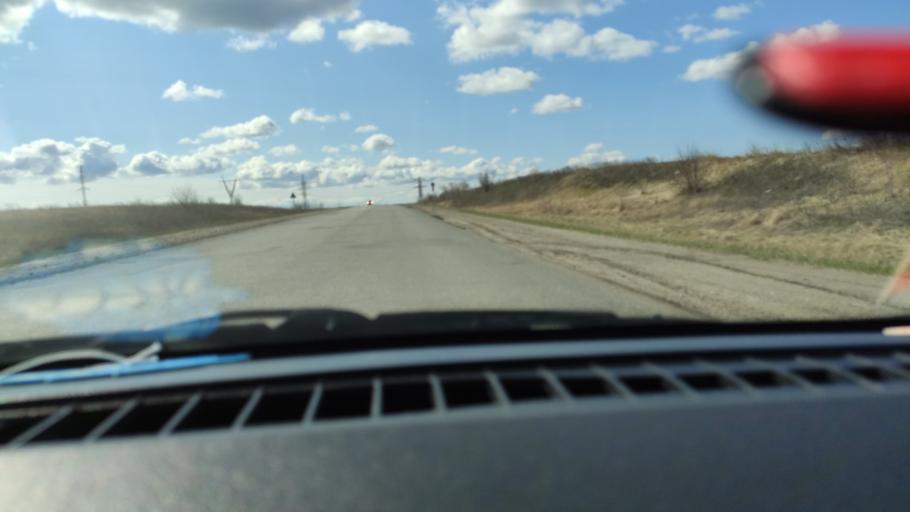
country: RU
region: Samara
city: Varlamovo
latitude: 53.0833
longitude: 48.3545
